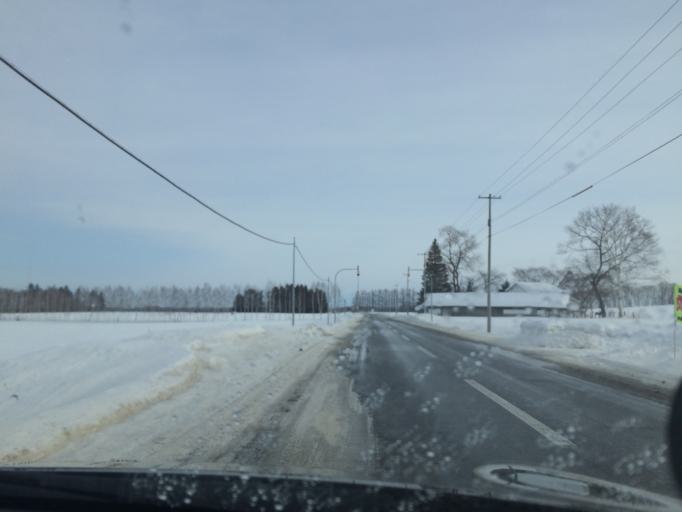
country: JP
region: Hokkaido
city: Obihiro
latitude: 42.9064
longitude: 142.9959
